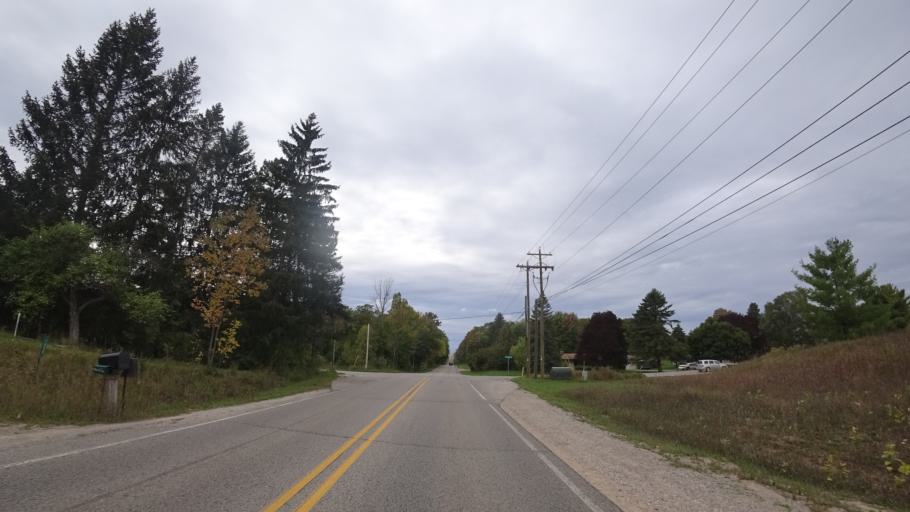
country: US
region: Michigan
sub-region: Emmet County
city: Petoskey
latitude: 45.3411
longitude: -84.9750
